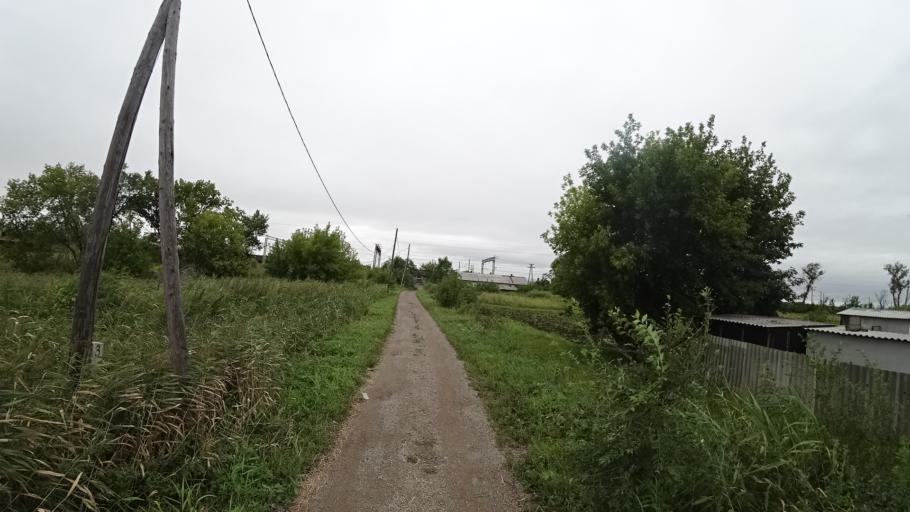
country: RU
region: Primorskiy
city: Chernigovka
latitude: 44.3412
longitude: 132.5381
